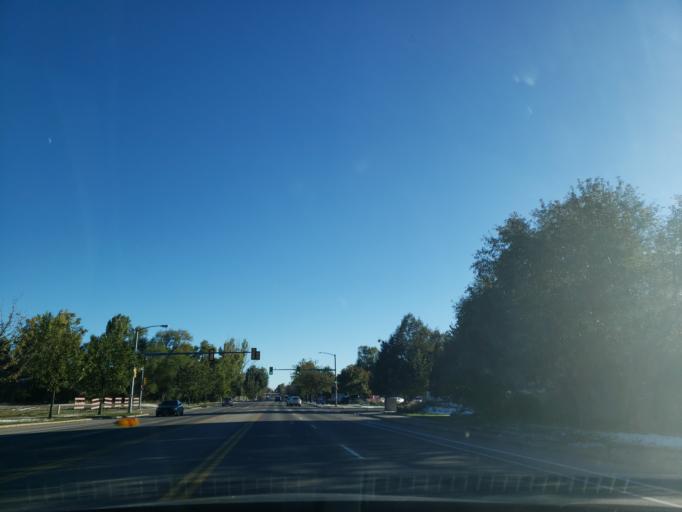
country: US
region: Colorado
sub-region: Larimer County
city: Fort Collins
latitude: 40.5644
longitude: -105.0961
